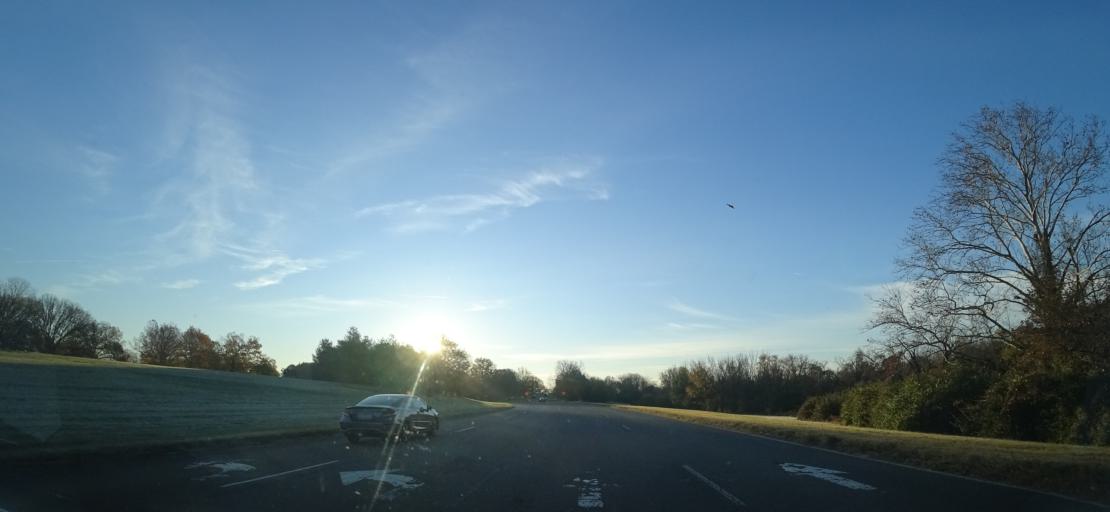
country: US
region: Washington, D.C.
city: Washington, D.C.
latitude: 38.8839
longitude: -77.0601
